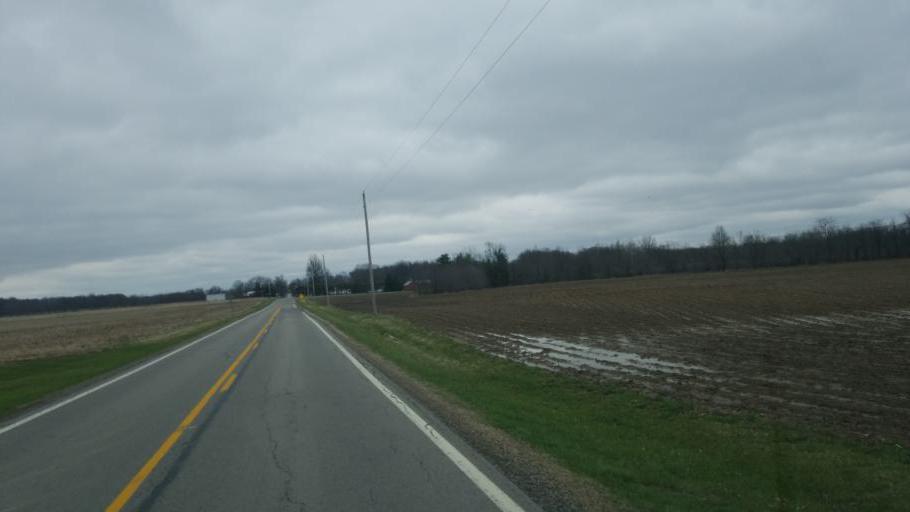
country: US
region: Ohio
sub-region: Hardin County
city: Forest
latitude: 40.6821
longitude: -83.3852
